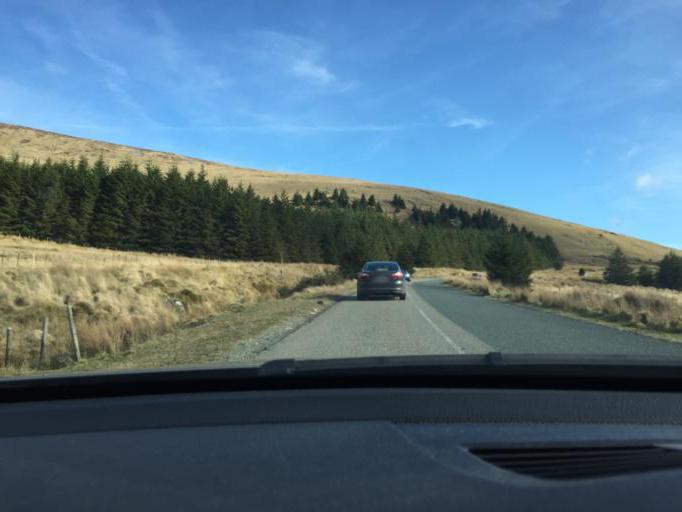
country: IE
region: Leinster
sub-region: Wicklow
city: Valleymount
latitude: 53.0545
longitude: -6.4094
